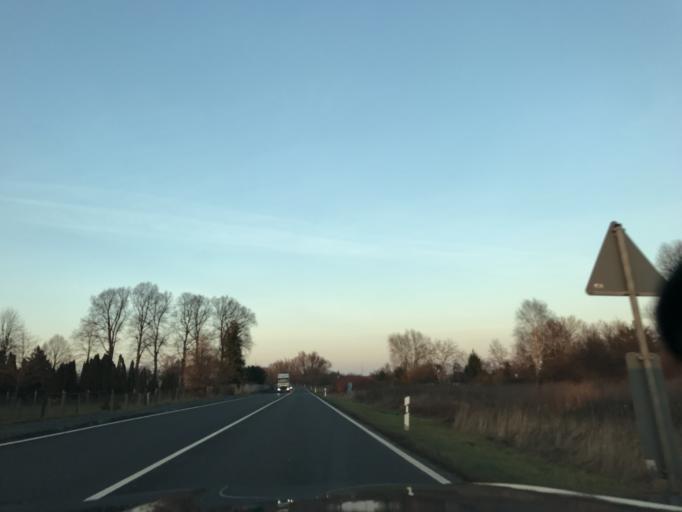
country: DE
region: Brandenburg
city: Nennhausen
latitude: 52.4941
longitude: 12.4586
